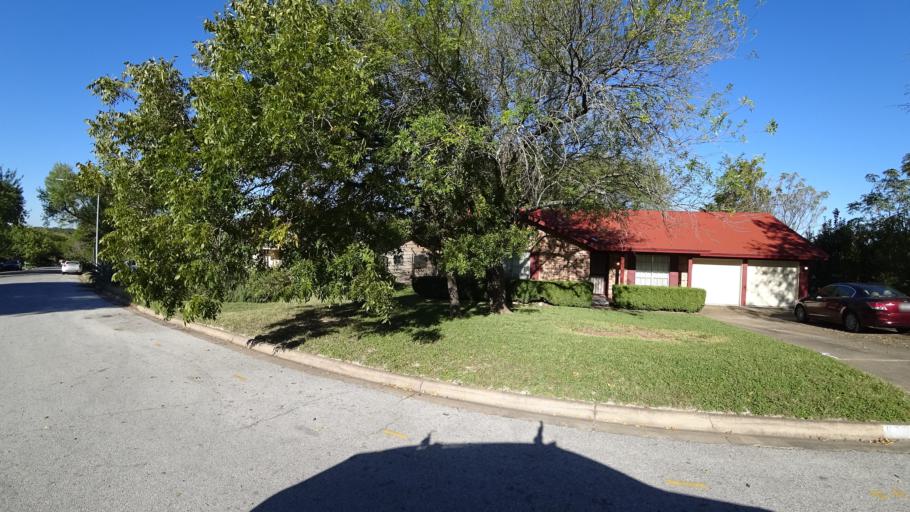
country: US
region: Texas
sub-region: Travis County
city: Austin
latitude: 30.3089
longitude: -97.6637
